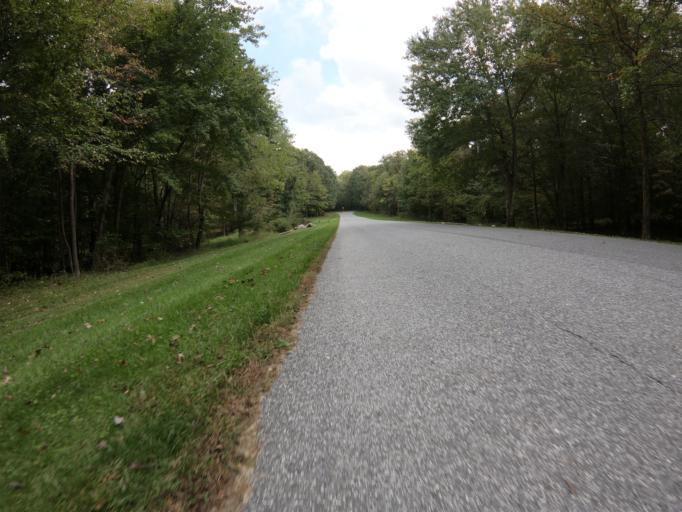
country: US
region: Maryland
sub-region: Howard County
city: Columbia
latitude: 39.2574
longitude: -76.8755
